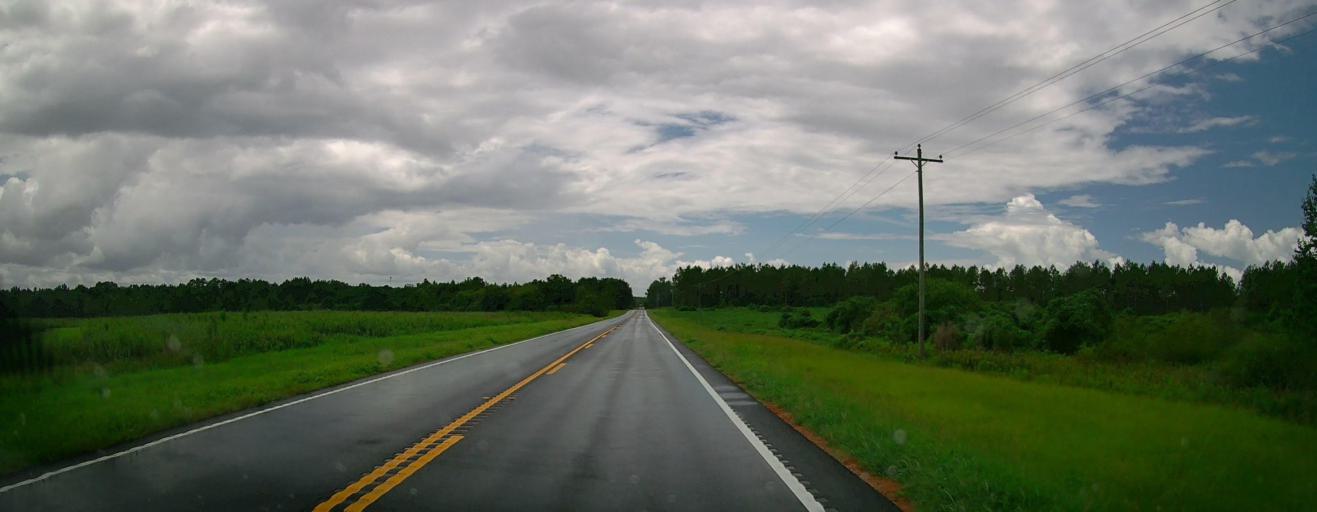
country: US
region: Georgia
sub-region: Pulaski County
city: Hawkinsville
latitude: 32.1741
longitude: -83.5376
